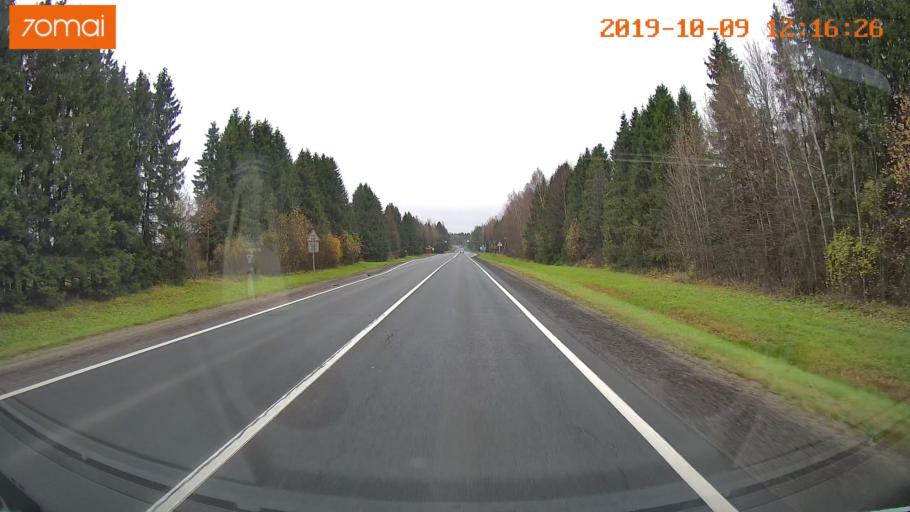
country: RU
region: Jaroslavl
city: Prechistoye
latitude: 58.4685
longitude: 40.3211
